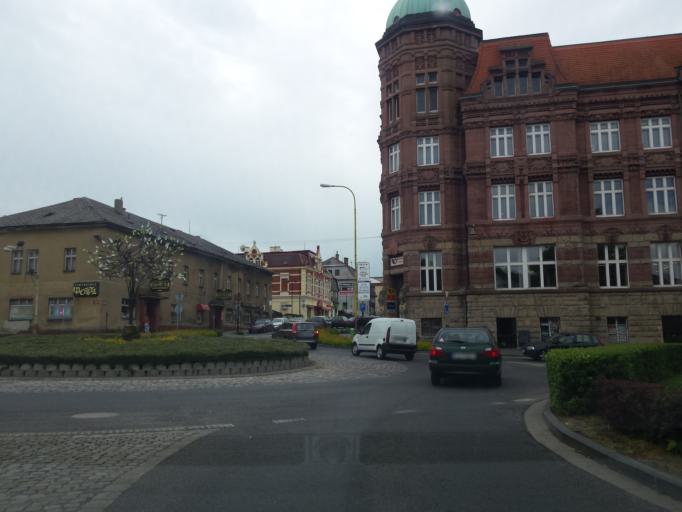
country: CZ
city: Novy Bor
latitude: 50.7592
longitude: 14.5562
